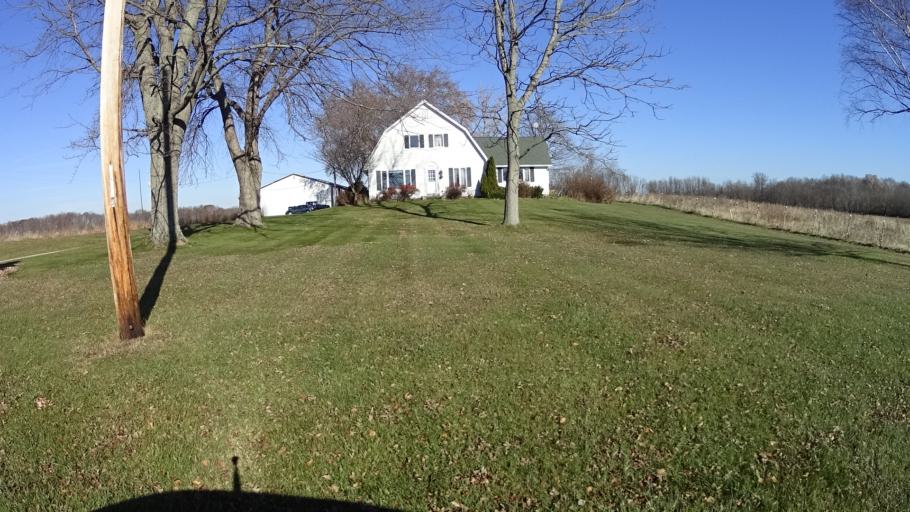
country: US
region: Ohio
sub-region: Huron County
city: New London
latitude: 41.0658
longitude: -82.3376
